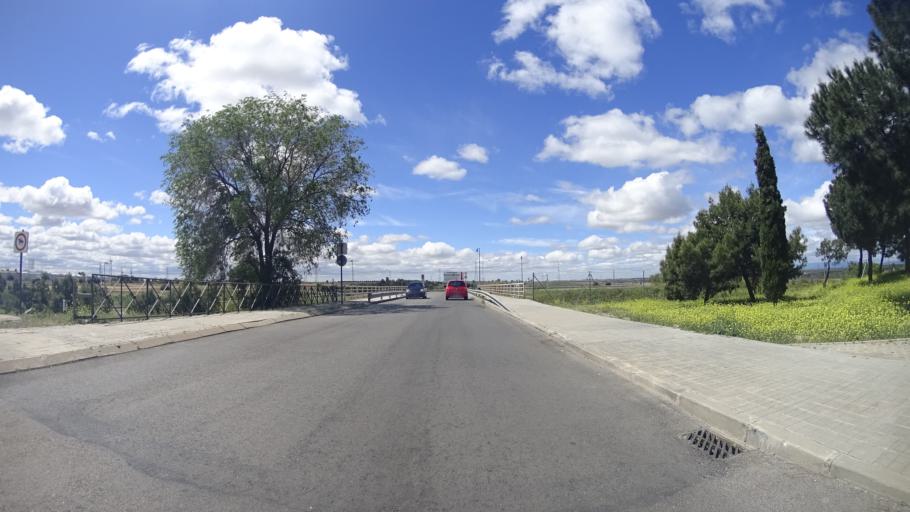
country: ES
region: Madrid
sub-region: Provincia de Madrid
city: Villaviciosa de Odon
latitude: 40.3532
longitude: -3.9114
